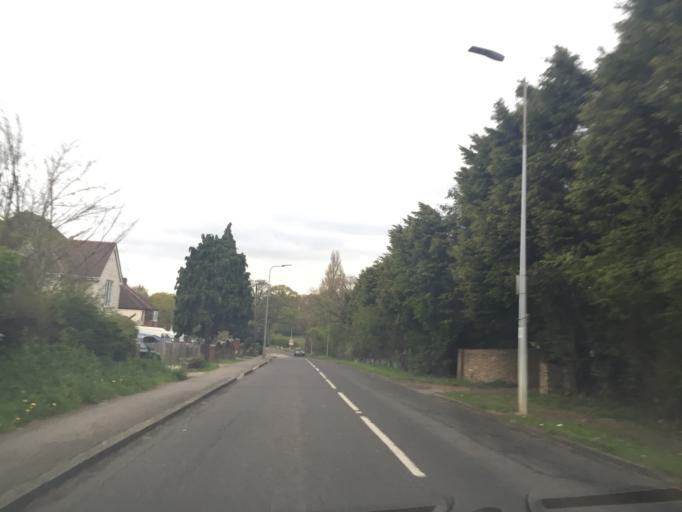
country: GB
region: England
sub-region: Greater London
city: Collier Row
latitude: 51.6231
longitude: 0.1874
